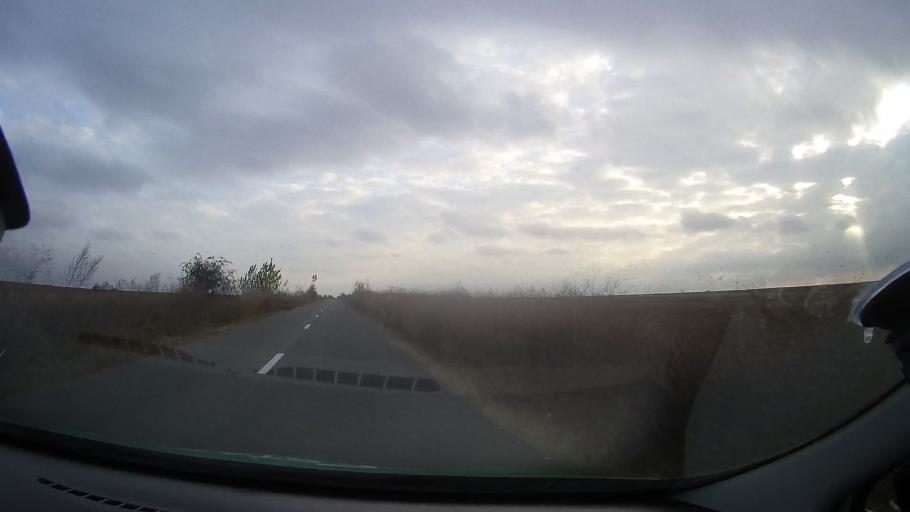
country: RO
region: Constanta
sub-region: Comuna Pestera
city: Pestera
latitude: 44.1425
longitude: 28.1165
